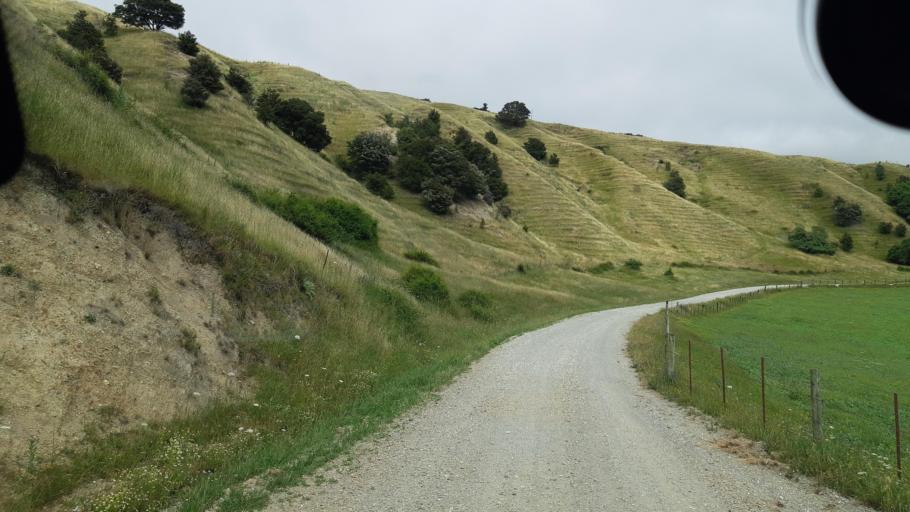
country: NZ
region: Marlborough
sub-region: Marlborough District
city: Blenheim
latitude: -41.9744
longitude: 173.9968
